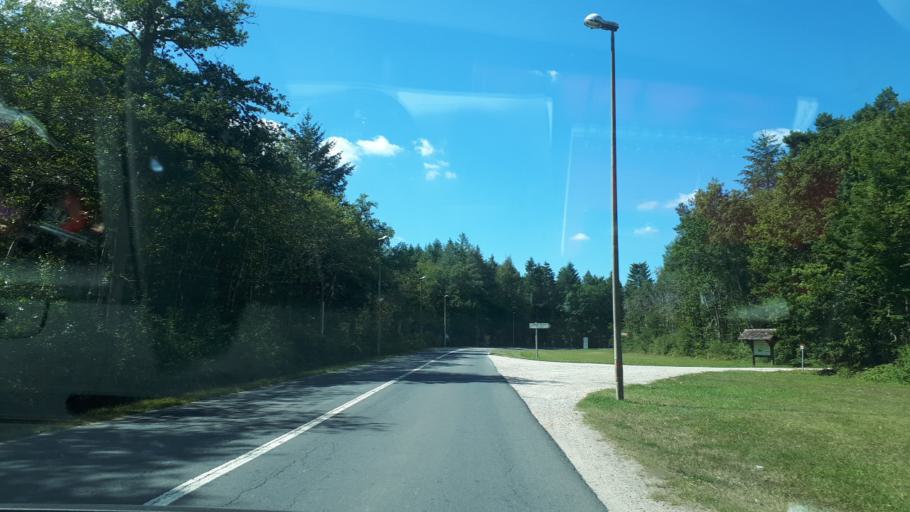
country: FR
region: Centre
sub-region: Departement du Loir-et-Cher
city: Lamotte-Beuvron
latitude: 47.5932
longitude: 2.0141
